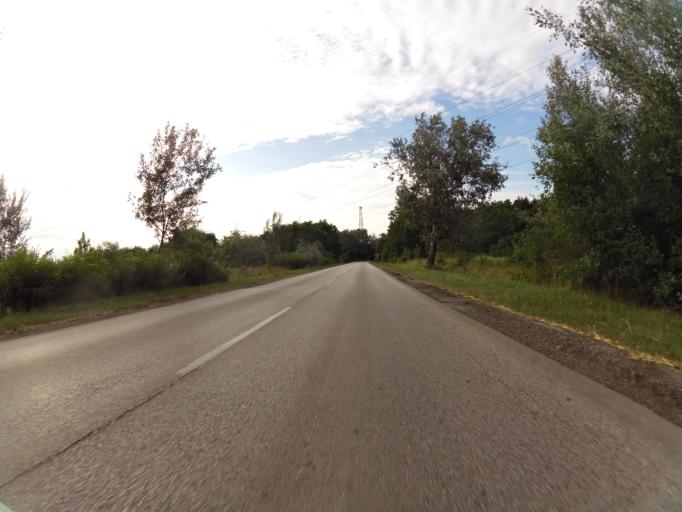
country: HU
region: Csongrad
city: Szeged
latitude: 46.3017
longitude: 20.1317
